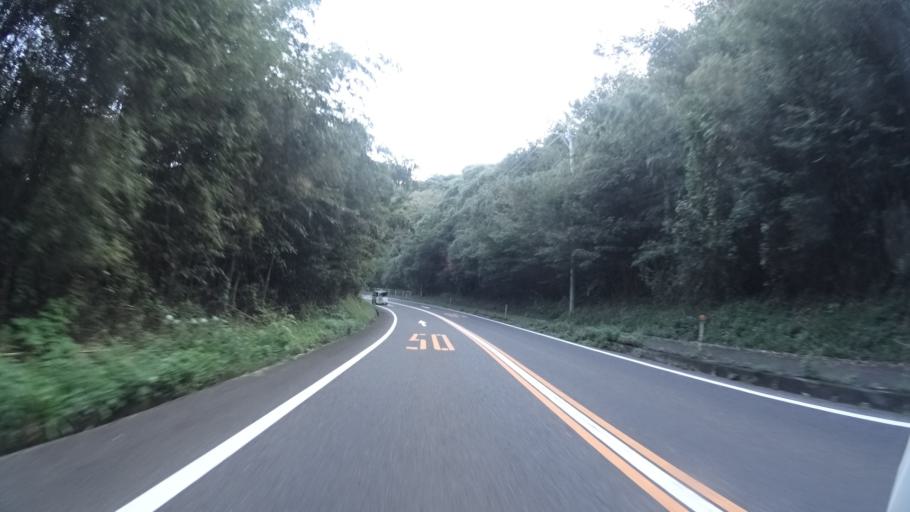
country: JP
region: Oita
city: Hiji
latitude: 33.3495
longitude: 131.4516
